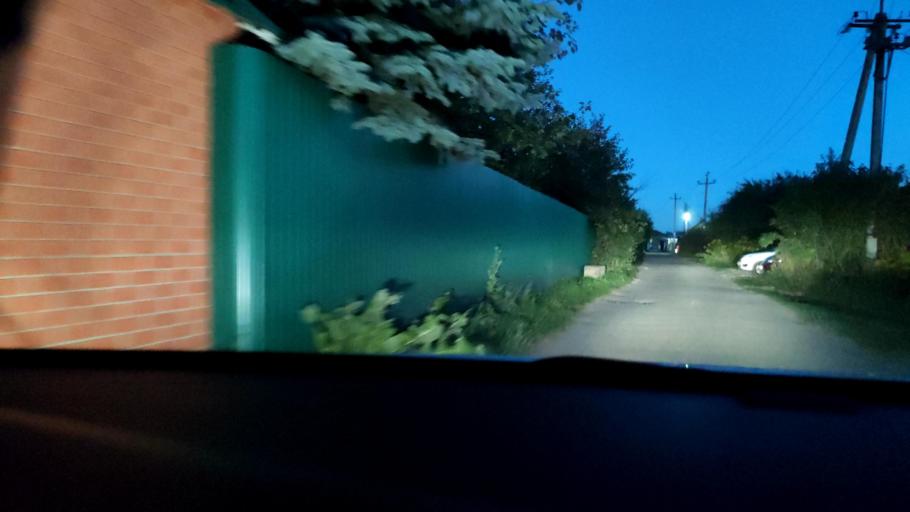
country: RU
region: Tatarstan
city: Vysokaya Gora
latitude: 55.8359
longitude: 49.2302
